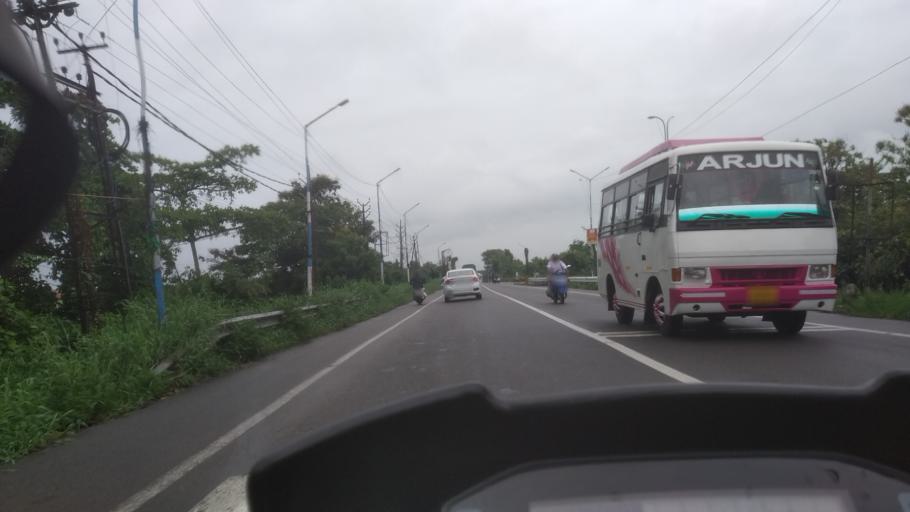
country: IN
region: Kerala
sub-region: Alappuzha
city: Kayankulam
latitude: 9.1720
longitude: 76.4974
